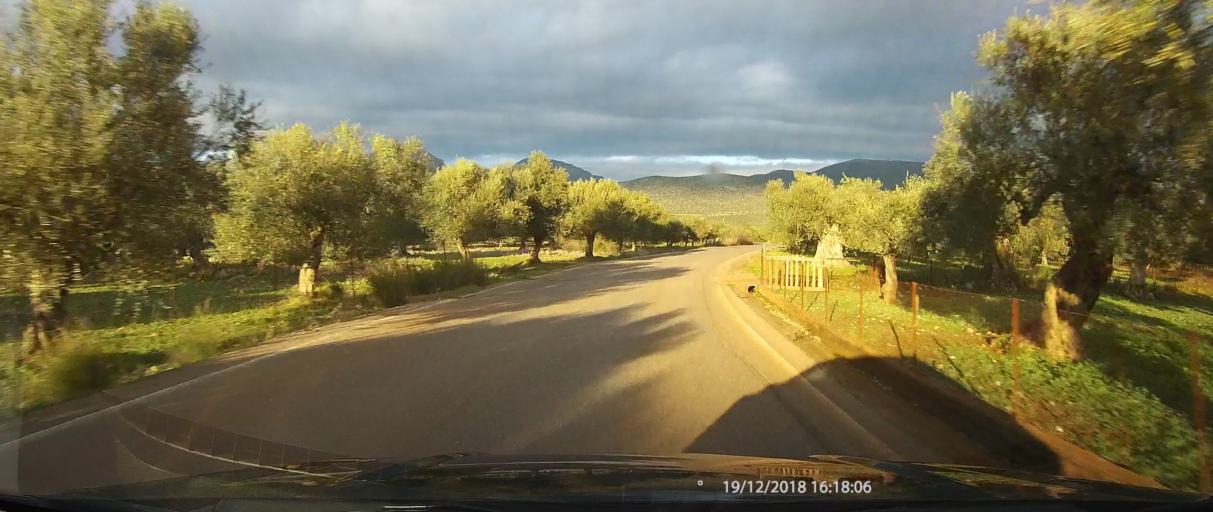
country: GR
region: Peloponnese
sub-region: Nomos Lakonias
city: Kato Glikovrisi
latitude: 36.9195
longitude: 22.8138
